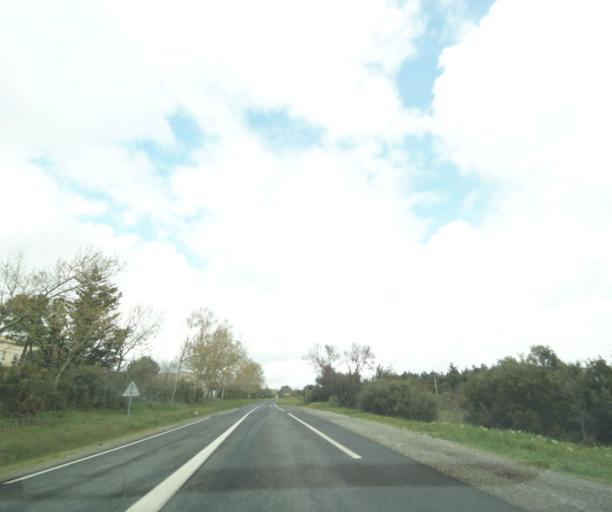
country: FR
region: Languedoc-Roussillon
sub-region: Departement de l'Herault
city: Cournonsec
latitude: 43.5413
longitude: 3.7007
